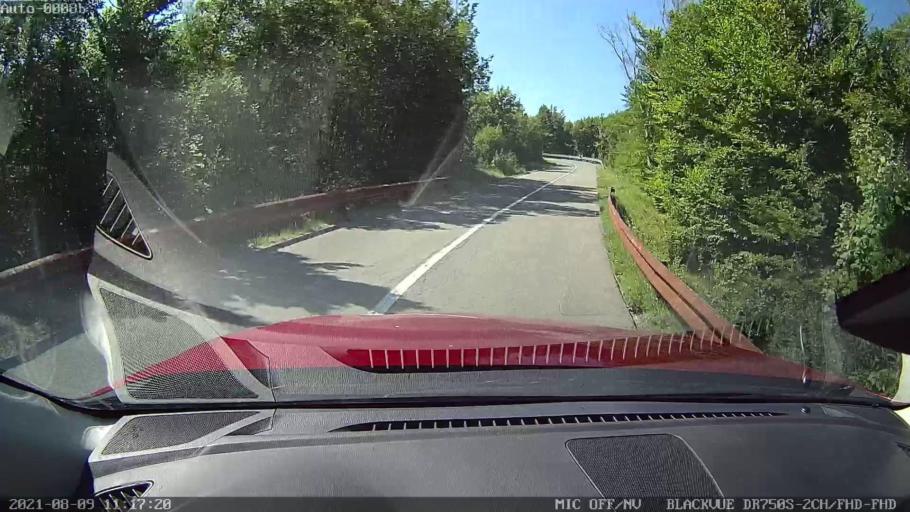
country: HR
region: Istarska
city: Lovran
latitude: 45.3126
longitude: 14.1894
